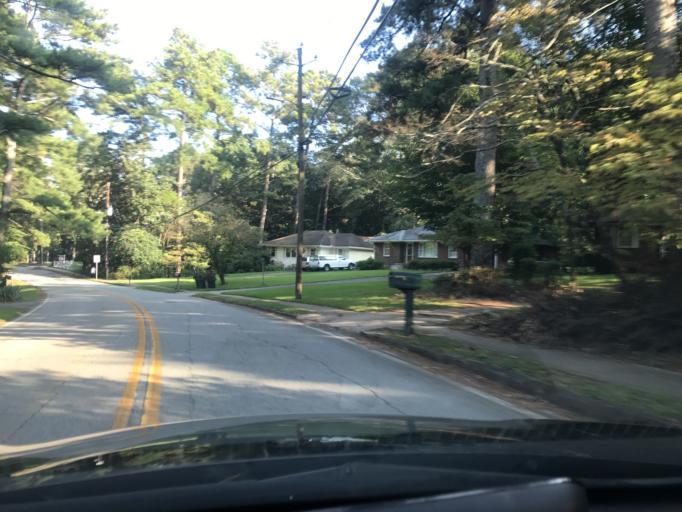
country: US
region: Georgia
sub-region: DeKalb County
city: North Druid Hills
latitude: 33.8270
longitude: -84.2799
